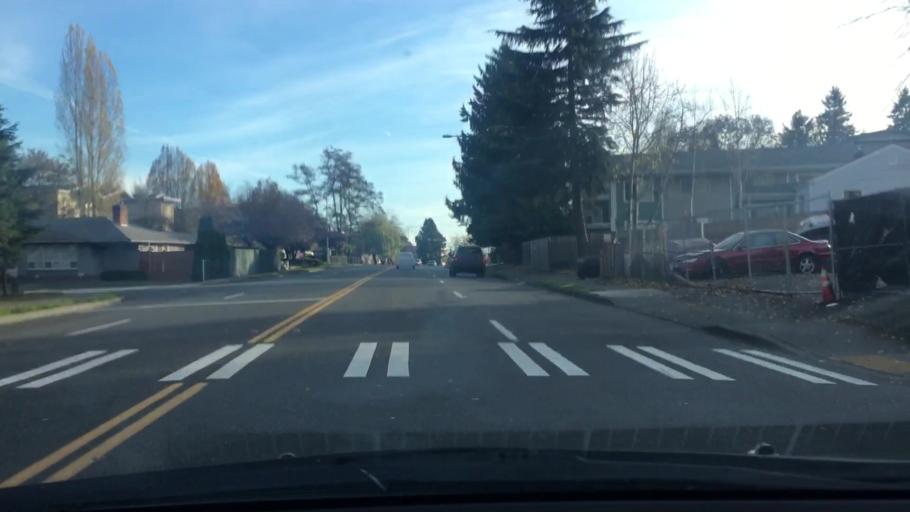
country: US
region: Washington
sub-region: King County
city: Burien
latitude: 47.4851
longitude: -122.3491
